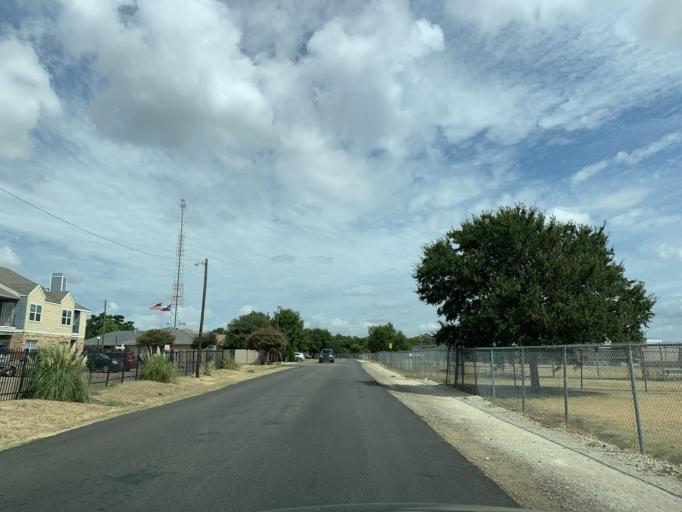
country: US
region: Texas
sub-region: Dallas County
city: Cockrell Hill
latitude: 32.7606
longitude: -96.8671
